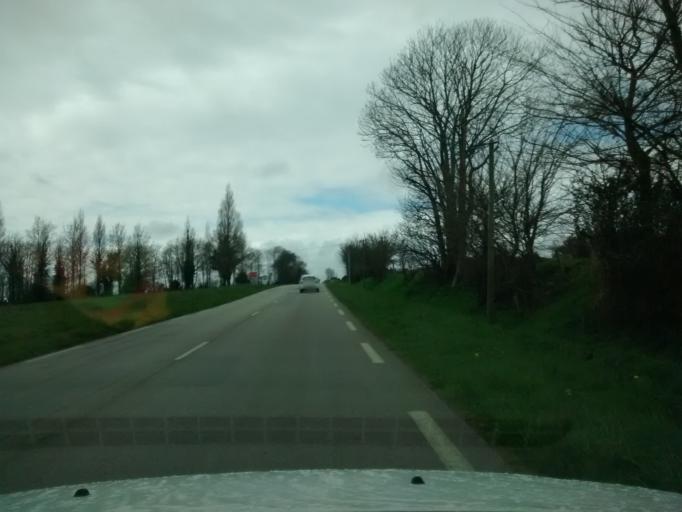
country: FR
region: Brittany
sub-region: Departement du Morbihan
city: Queven
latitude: 47.7712
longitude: -3.4098
